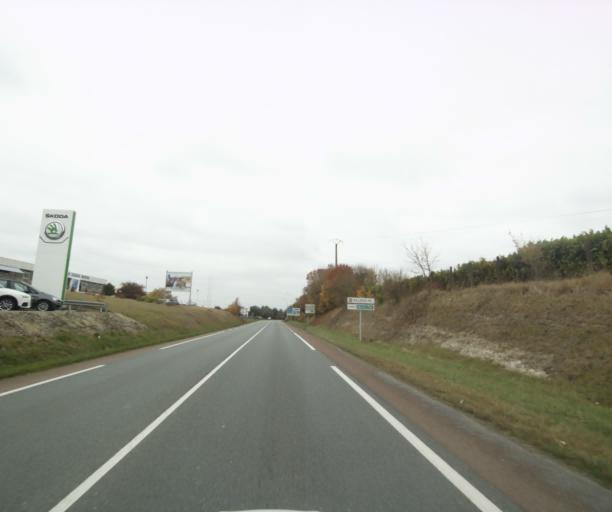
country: FR
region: Poitou-Charentes
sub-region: Departement de la Charente-Maritime
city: Les Gonds
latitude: 45.7210
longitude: -0.6378
